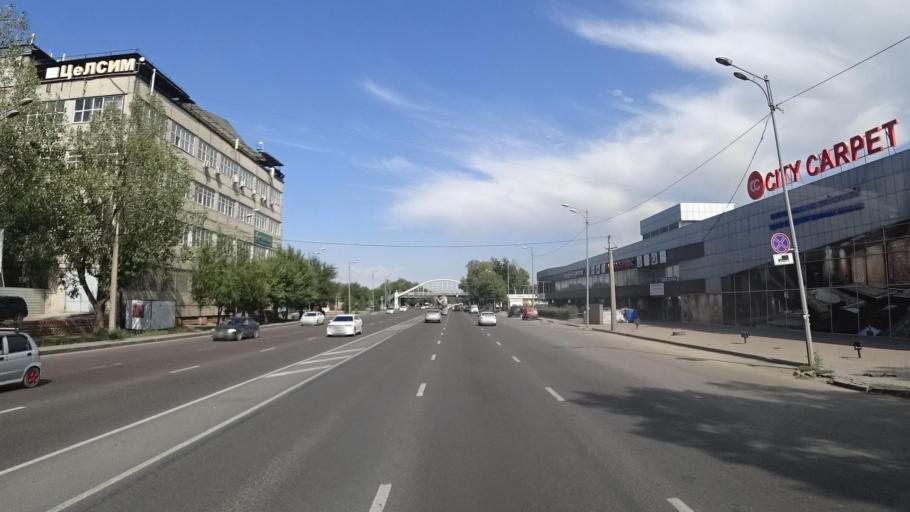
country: KZ
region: Almaty Qalasy
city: Almaty
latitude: 43.2750
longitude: 76.8933
